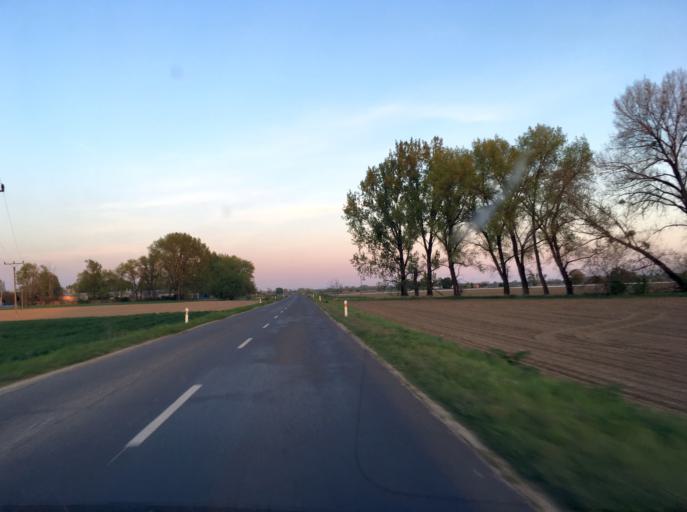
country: SK
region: Nitriansky
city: Kolarovo
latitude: 47.9230
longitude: 18.0312
